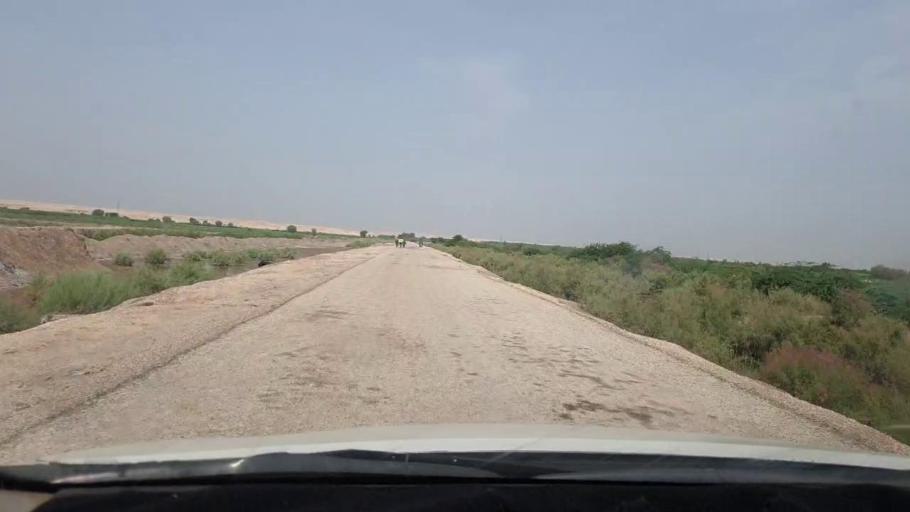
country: PK
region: Sindh
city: Rohri
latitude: 27.5950
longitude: 68.9967
